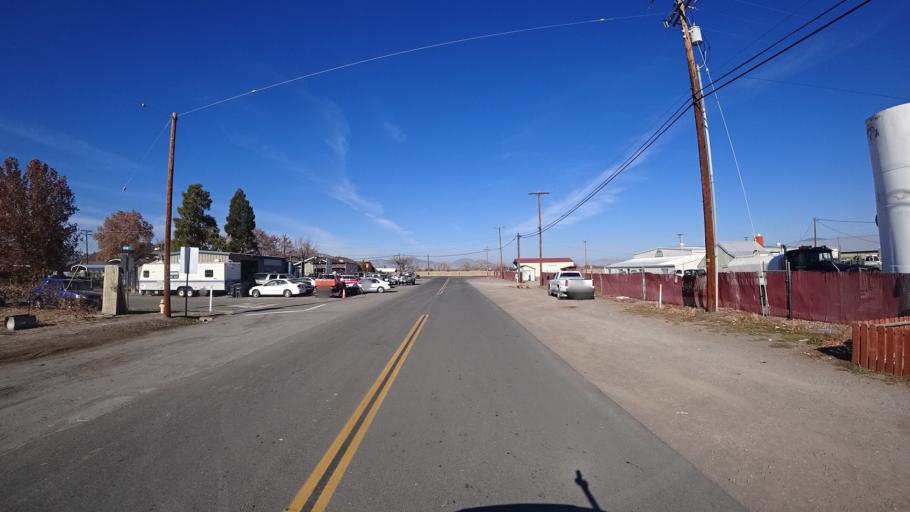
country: US
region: California
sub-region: Siskiyou County
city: Montague
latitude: 41.6461
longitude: -122.5224
